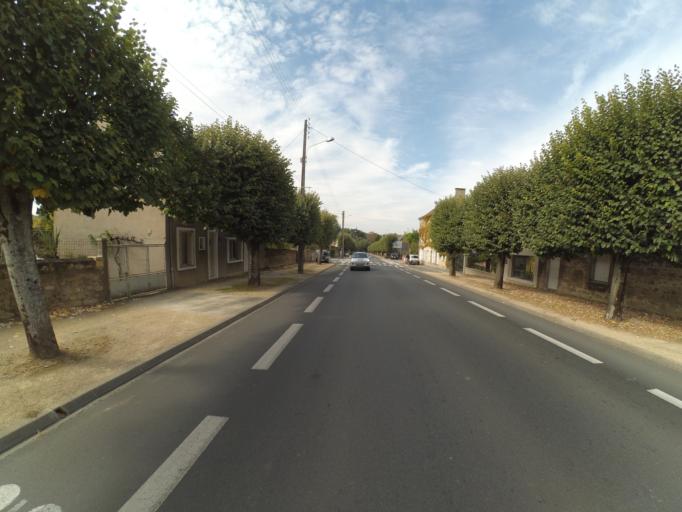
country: FR
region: Pays de la Loire
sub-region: Departement de Maine-et-Loire
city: Doue-la-Fontaine
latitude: 47.1968
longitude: -0.2708
